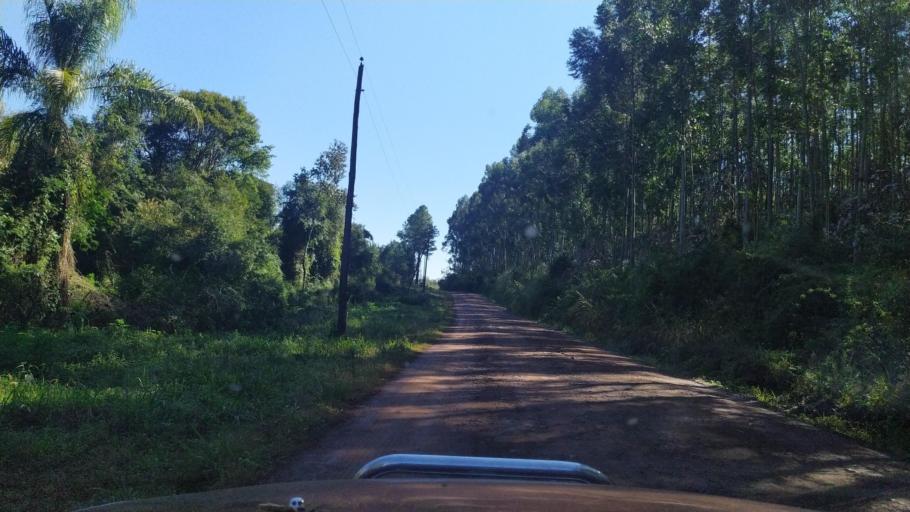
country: AR
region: Misiones
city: El Alcazar
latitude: -26.7195
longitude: -54.6895
